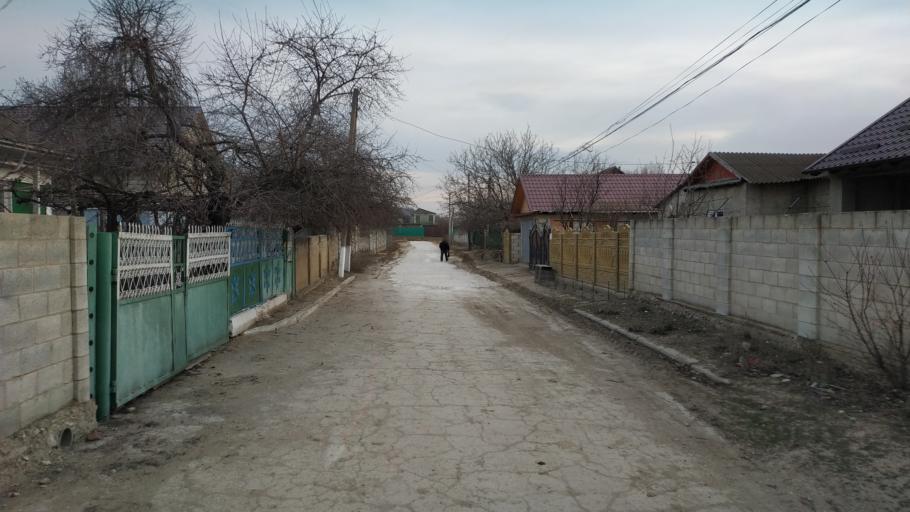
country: MD
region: Hincesti
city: Dancu
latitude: 46.7613
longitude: 28.2068
